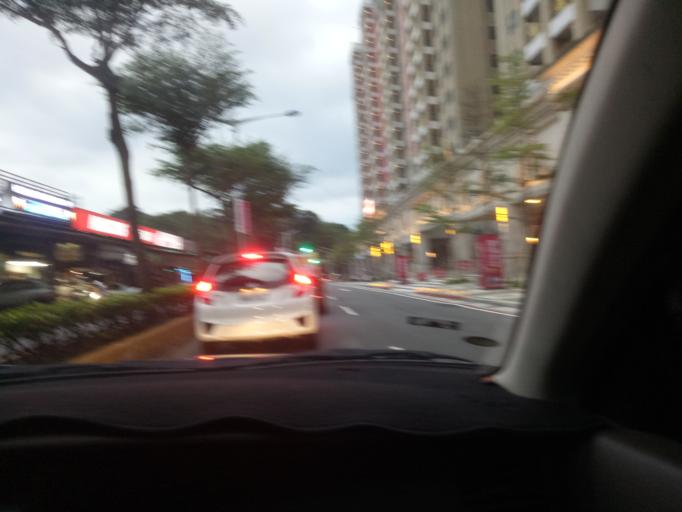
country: TW
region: Taiwan
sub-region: Keelung
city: Keelung
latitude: 25.1284
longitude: 121.7792
